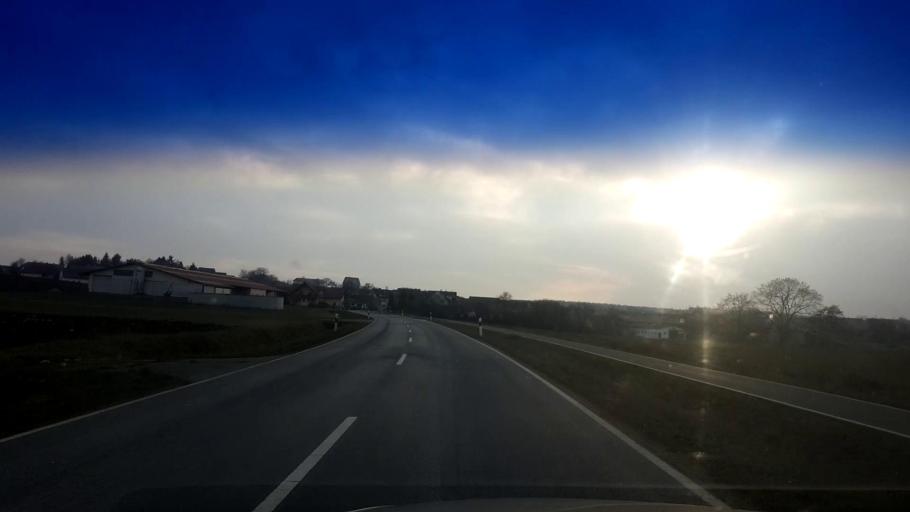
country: DE
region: Bavaria
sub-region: Upper Franconia
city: Hallerndorf
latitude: 49.7890
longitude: 10.9596
